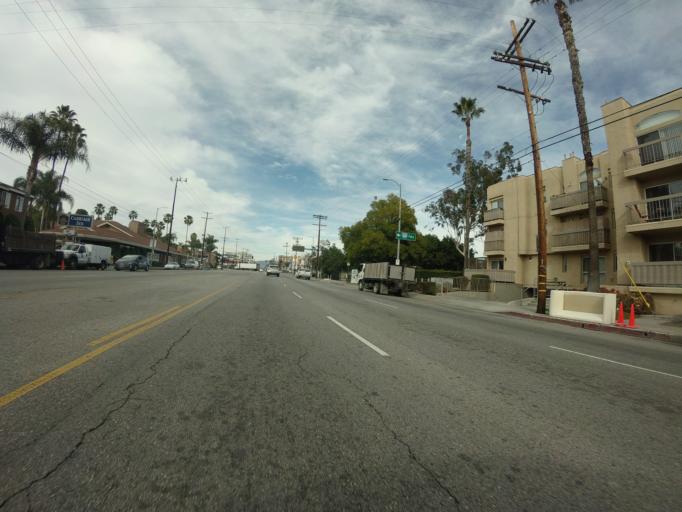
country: US
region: California
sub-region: Los Angeles County
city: Van Nuys
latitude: 34.1708
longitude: -118.4661
